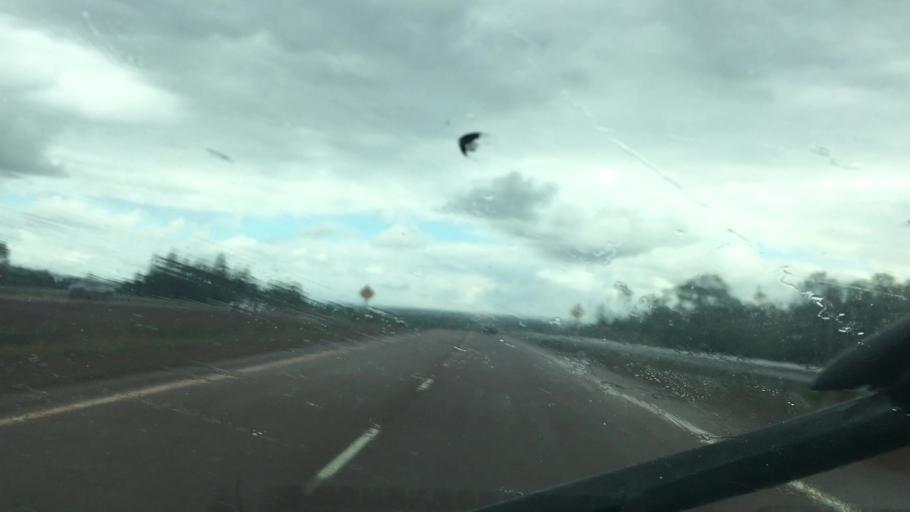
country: CA
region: Nova Scotia
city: Antigonish
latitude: 45.5949
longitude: -61.8773
